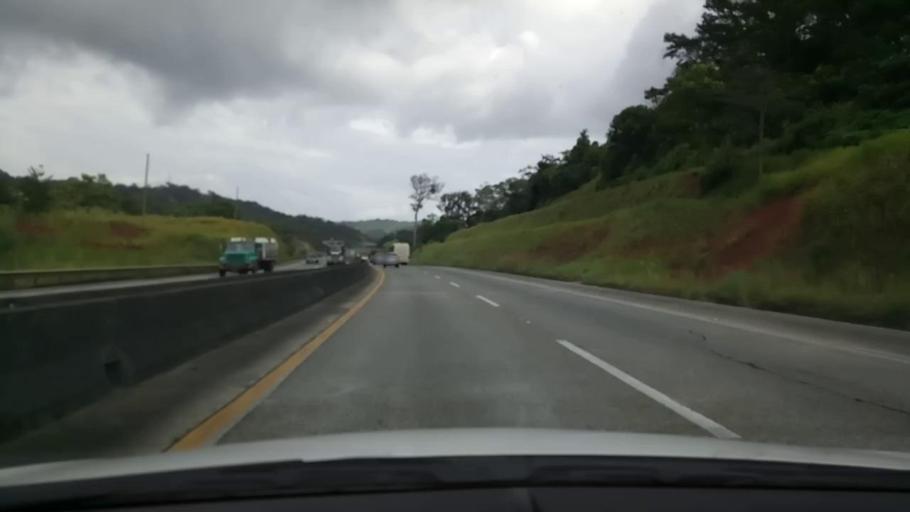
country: PA
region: Colon
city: Gatun
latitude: 9.2827
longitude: -79.7742
